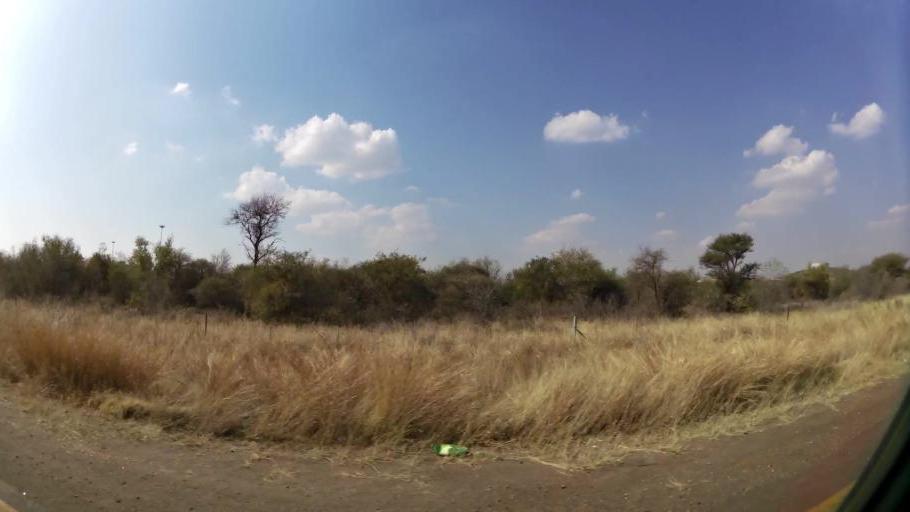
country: ZA
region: North-West
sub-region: Bojanala Platinum District Municipality
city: Mogwase
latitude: -25.4232
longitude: 27.0799
